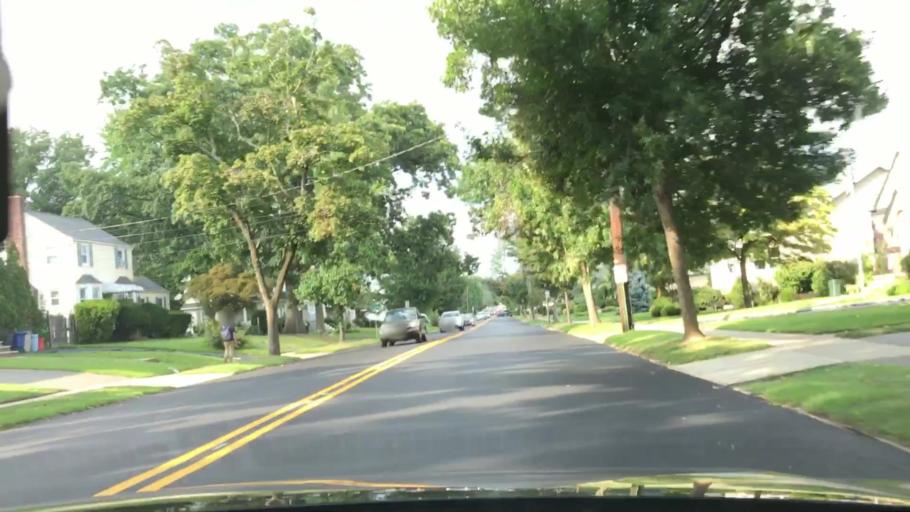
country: US
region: New Jersey
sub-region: Bergen County
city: Maywood
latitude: 40.9080
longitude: -74.0594
